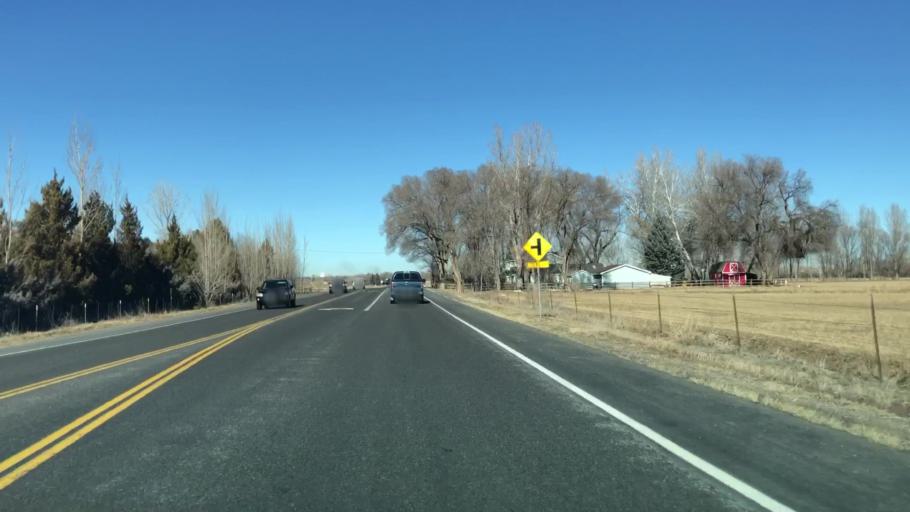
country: US
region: Colorado
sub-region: Weld County
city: Windsor
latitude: 40.5070
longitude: -104.9818
